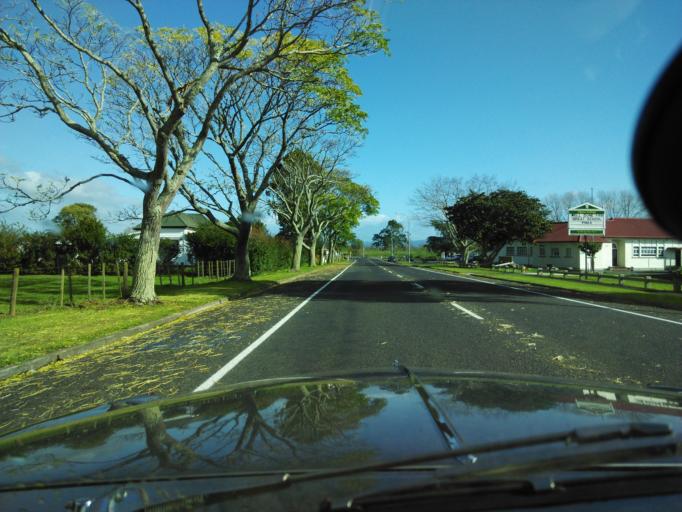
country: NZ
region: Waikato
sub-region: Hauraki District
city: Paeroa
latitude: -37.3854
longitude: 175.6701
